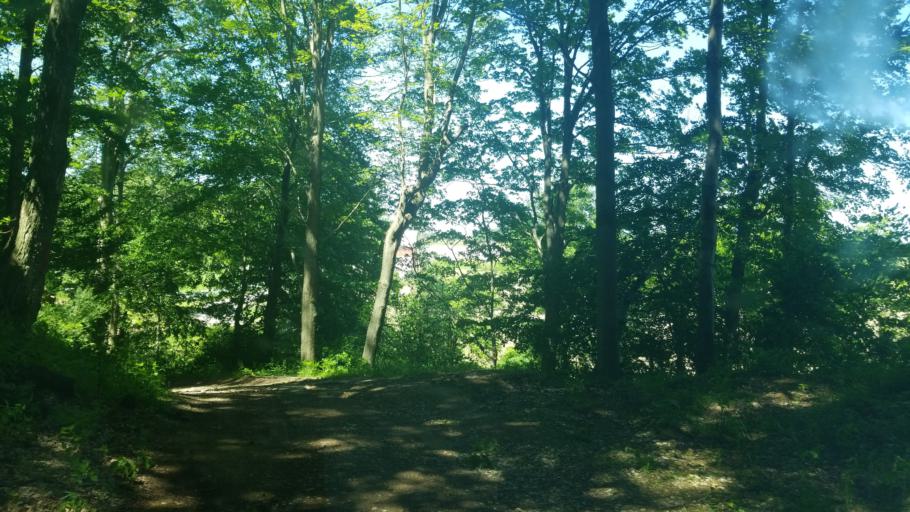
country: US
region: Ohio
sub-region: Sandusky County
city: Bellville
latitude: 40.6032
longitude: -82.5775
